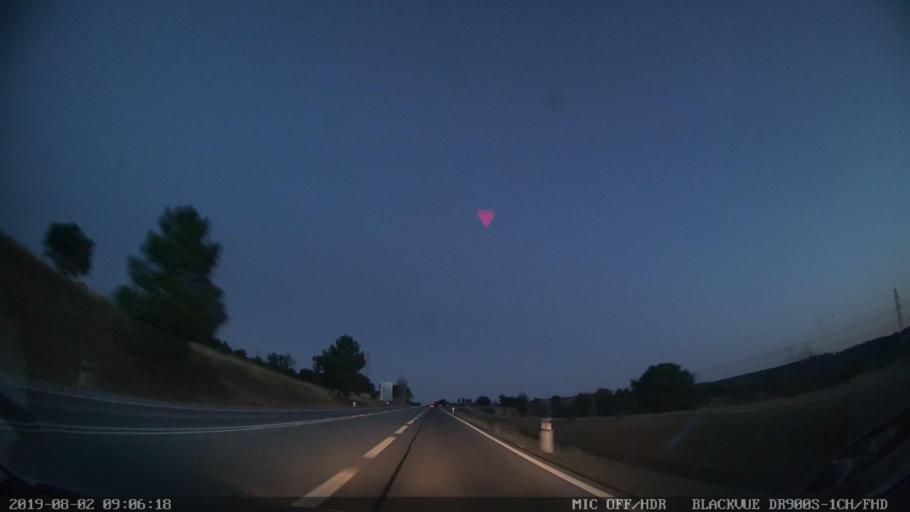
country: PT
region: Portalegre
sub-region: Nisa
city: Nisa
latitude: 39.5287
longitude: -7.7870
